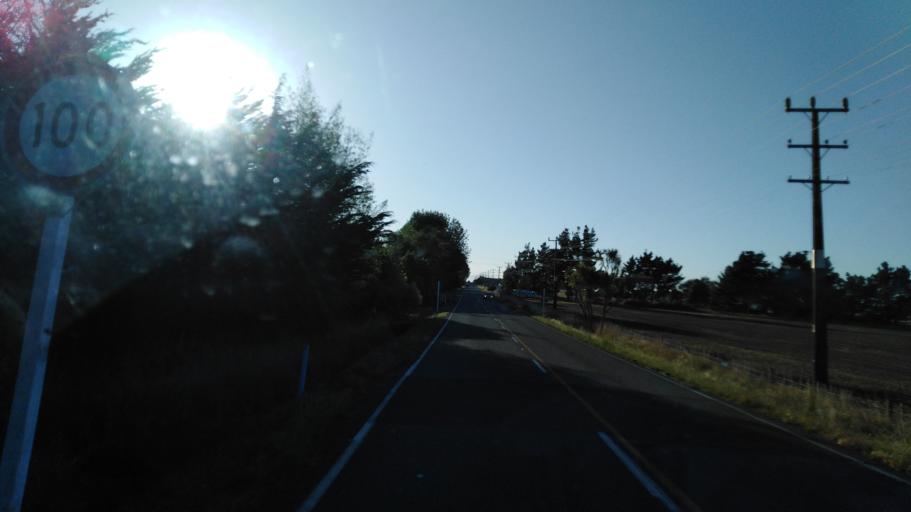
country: NZ
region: Manawatu-Wanganui
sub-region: Rangitikei District
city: Bulls
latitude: -40.0671
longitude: 175.4015
